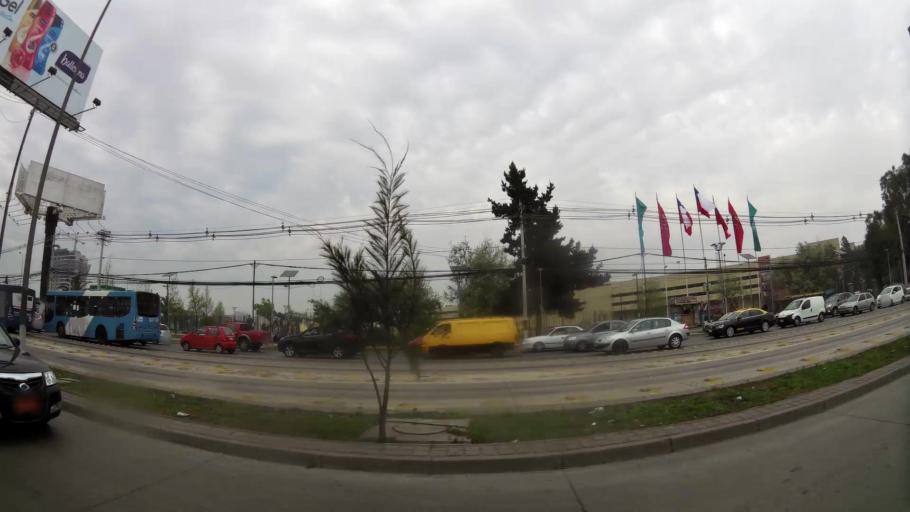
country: CL
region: Santiago Metropolitan
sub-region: Provincia de Santiago
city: Villa Presidente Frei, Nunoa, Santiago, Chile
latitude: -33.5091
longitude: -70.6052
